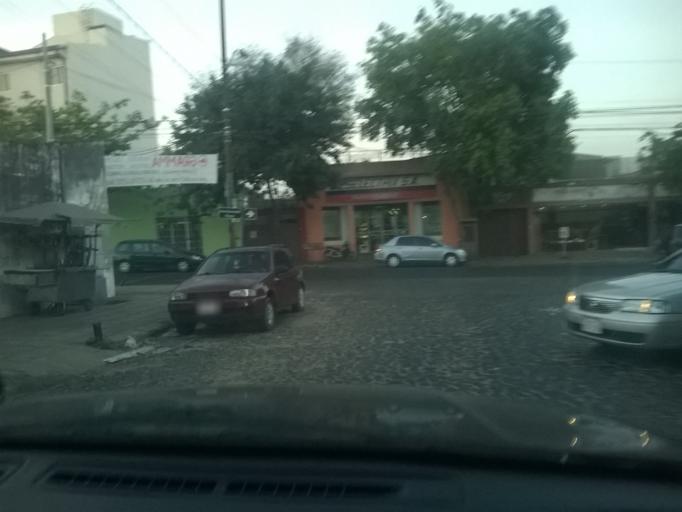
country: PY
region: Asuncion
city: Asuncion
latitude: -25.3062
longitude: -57.6008
